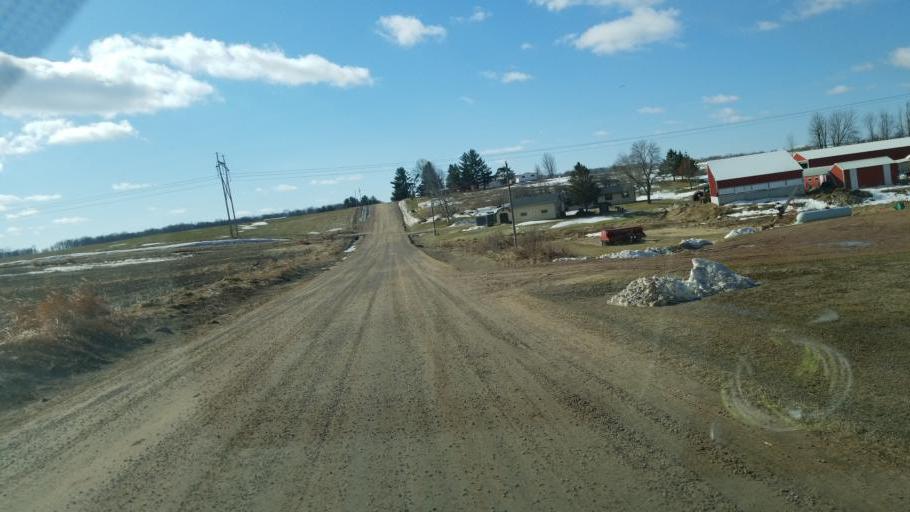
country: US
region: Wisconsin
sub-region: Clark County
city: Loyal
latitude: 44.6709
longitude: -90.4559
